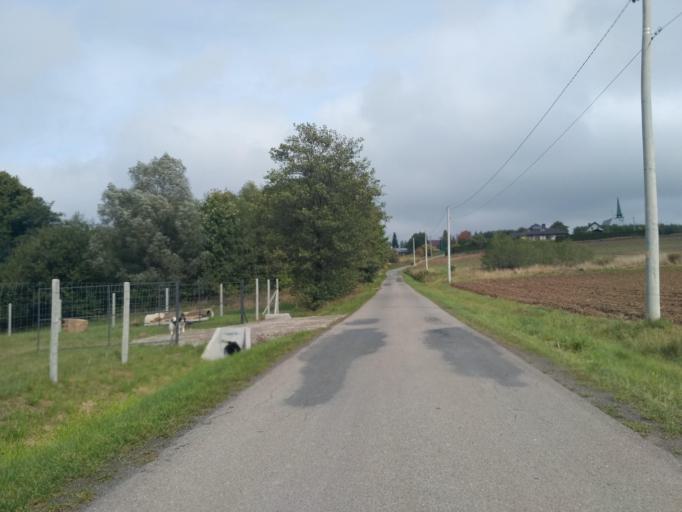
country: PL
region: Subcarpathian Voivodeship
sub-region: Powiat ropczycko-sedziszowski
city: Niedzwiada
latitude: 49.9607
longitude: 21.4420
